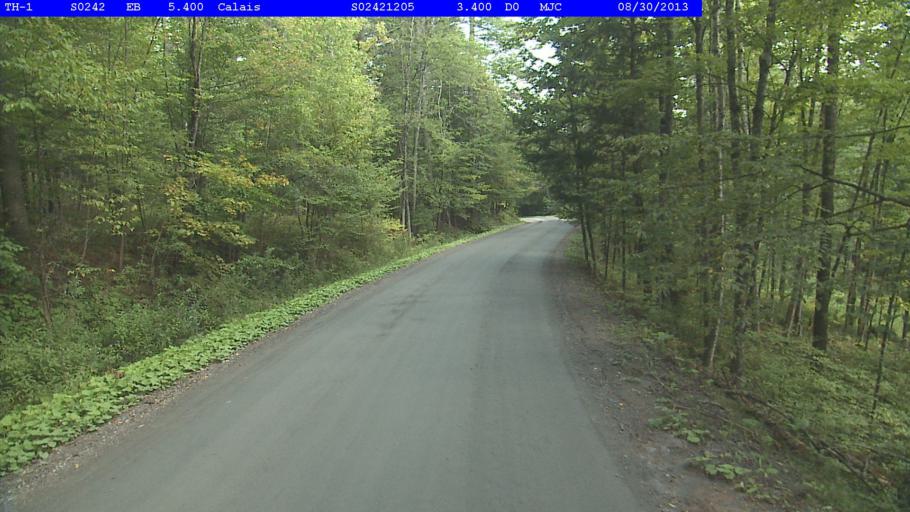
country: US
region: Vermont
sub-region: Washington County
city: Montpelier
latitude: 44.3664
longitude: -72.4791
